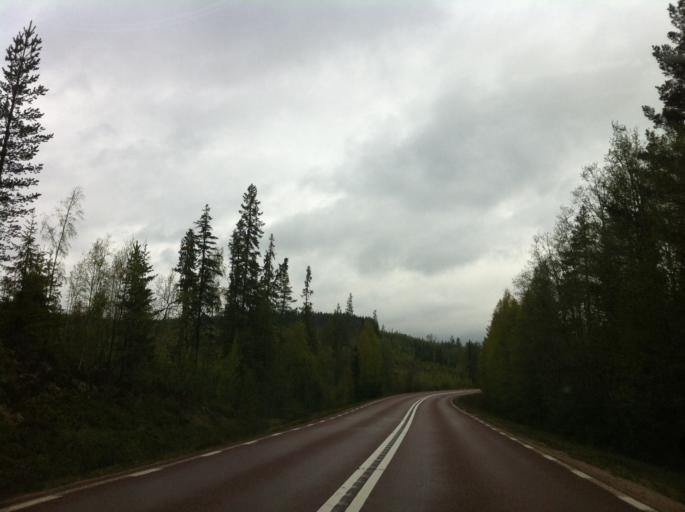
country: SE
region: Jaemtland
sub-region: Harjedalens Kommun
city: Sveg
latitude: 61.8722
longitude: 14.6309
